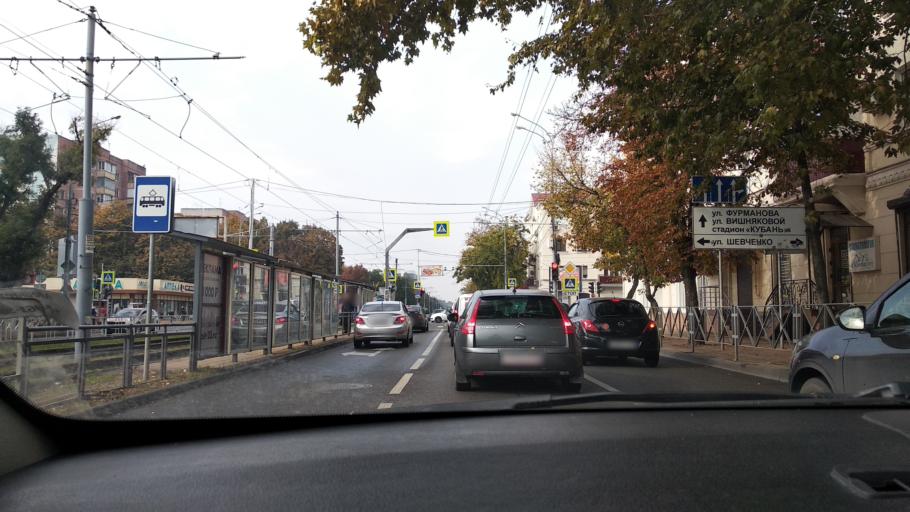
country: RU
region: Krasnodarskiy
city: Krasnodar
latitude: 45.0209
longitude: 39.0108
